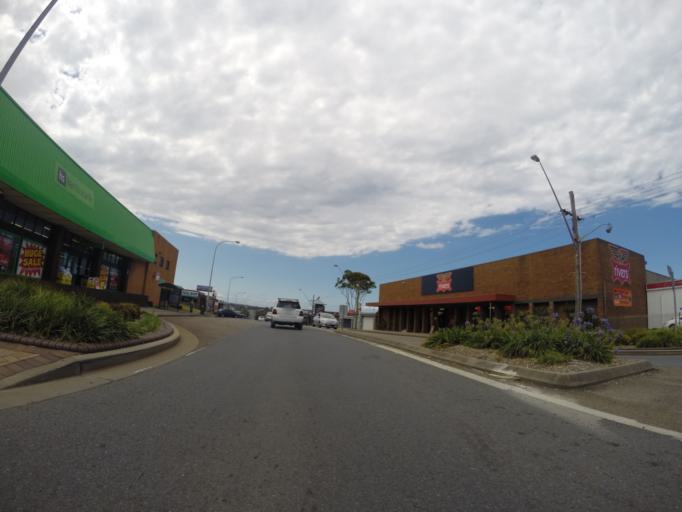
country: AU
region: New South Wales
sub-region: Shoalhaven Shire
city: Ulladulla
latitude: -35.3626
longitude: 150.4731
